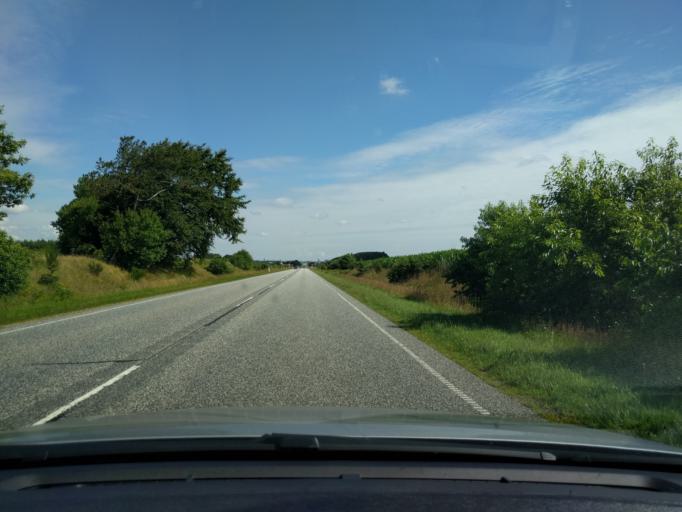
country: DK
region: Central Jutland
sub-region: Herning Kommune
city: Snejbjerg
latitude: 56.0877
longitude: 8.9222
